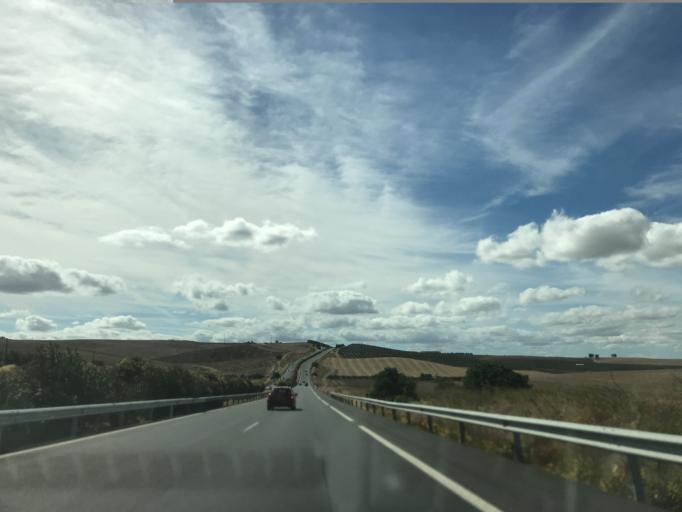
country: ES
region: Andalusia
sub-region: Province of Cordoba
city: La Victoria
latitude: 37.7366
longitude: -4.8510
